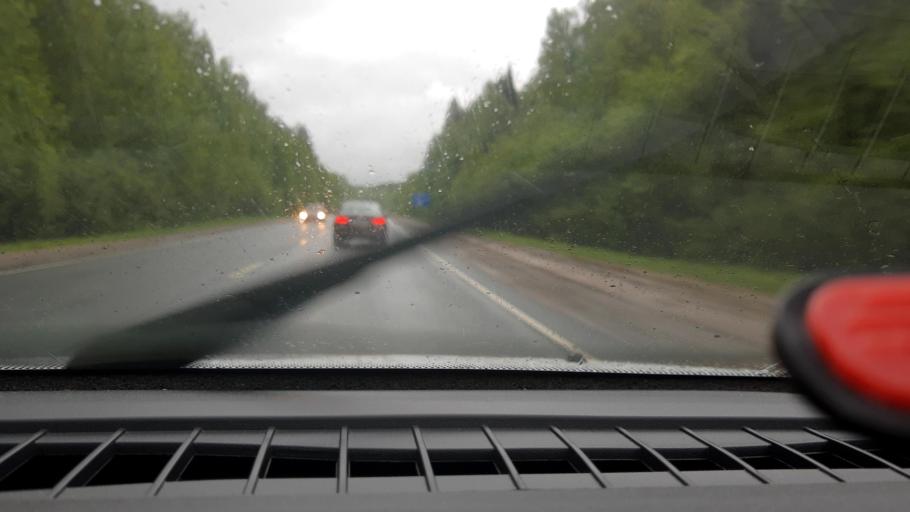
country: RU
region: Nizjnij Novgorod
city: Semenov
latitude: 56.7638
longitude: 44.3906
